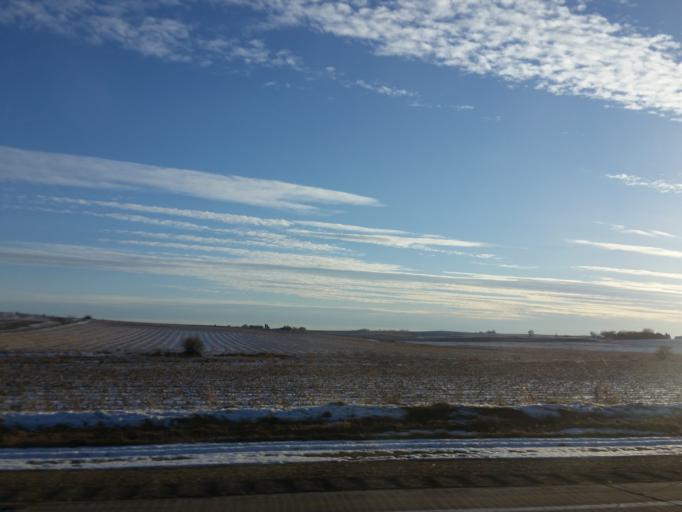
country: US
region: Iowa
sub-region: Butler County
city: Allison
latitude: 42.7449
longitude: -92.8553
